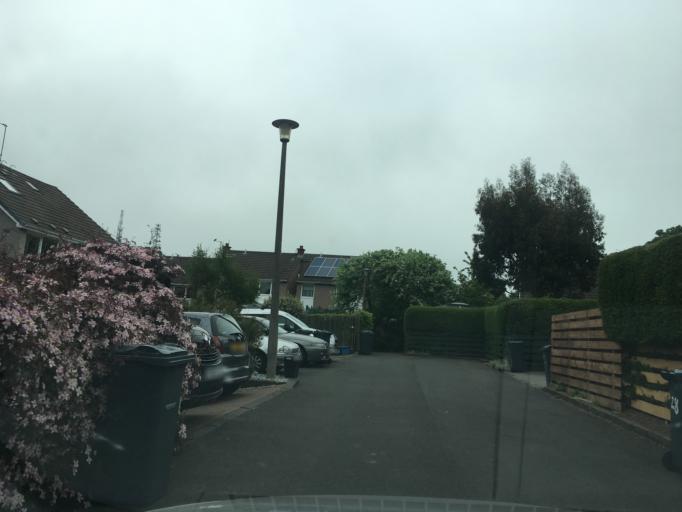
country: GB
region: Scotland
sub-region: Edinburgh
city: Edinburgh
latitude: 55.9083
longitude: -3.2055
